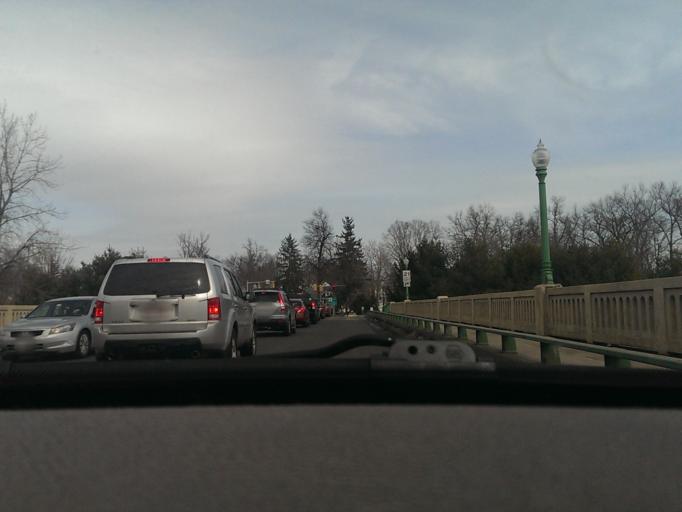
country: US
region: Massachusetts
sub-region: Hampden County
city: Ludlow
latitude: 42.1564
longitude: -72.4848
